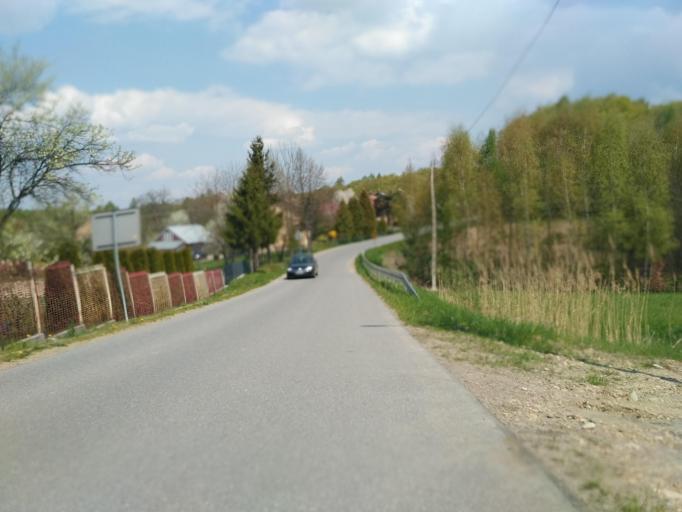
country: PL
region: Subcarpathian Voivodeship
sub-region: Powiat jasielski
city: Debowiec
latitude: 49.6981
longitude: 21.5074
